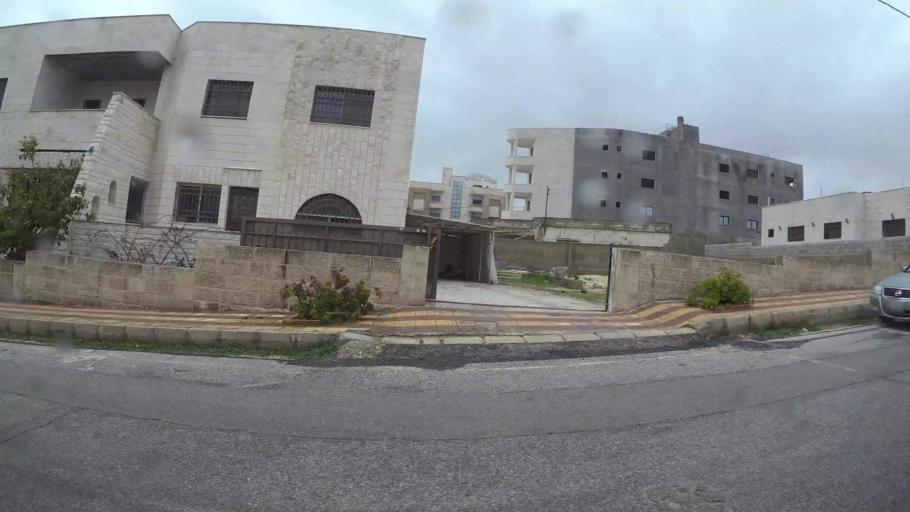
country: JO
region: Amman
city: Al Jubayhah
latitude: 31.9869
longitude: 35.8574
